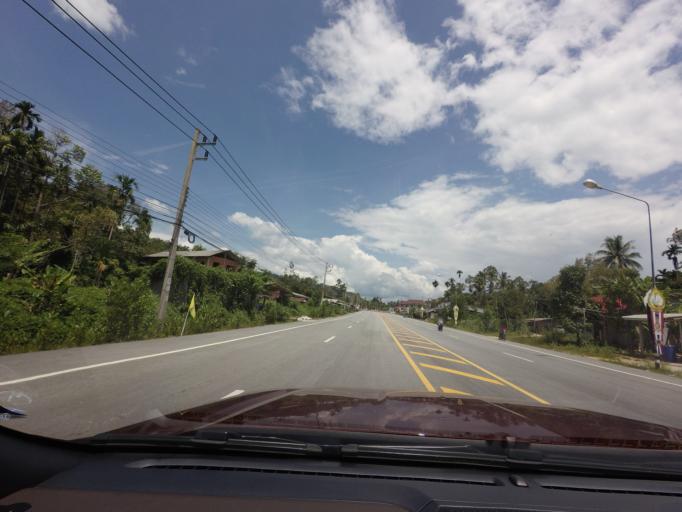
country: TH
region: Narathiwat
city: Chanae
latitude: 6.1019
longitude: 101.6922
